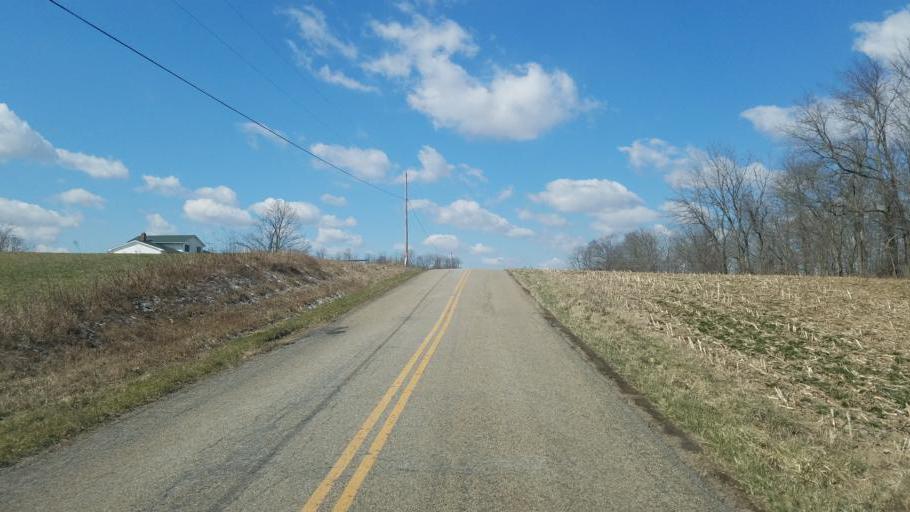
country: US
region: Ohio
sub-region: Licking County
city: Utica
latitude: 40.2661
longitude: -82.5091
